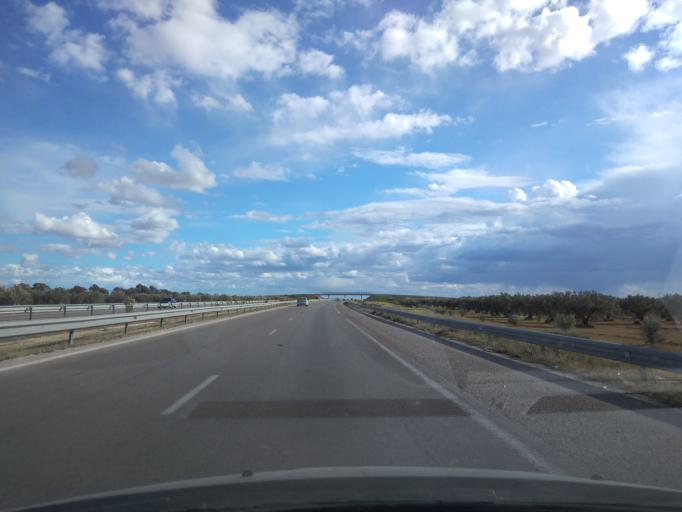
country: TN
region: Al Munastir
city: Manzil Kamil
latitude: 35.6232
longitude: 10.5934
